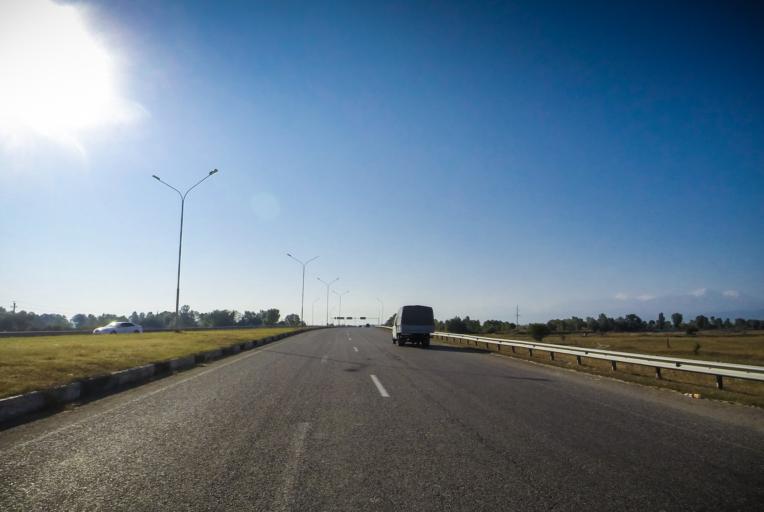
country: RU
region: North Ossetia
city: Ardon
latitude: 43.1773
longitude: 44.3192
